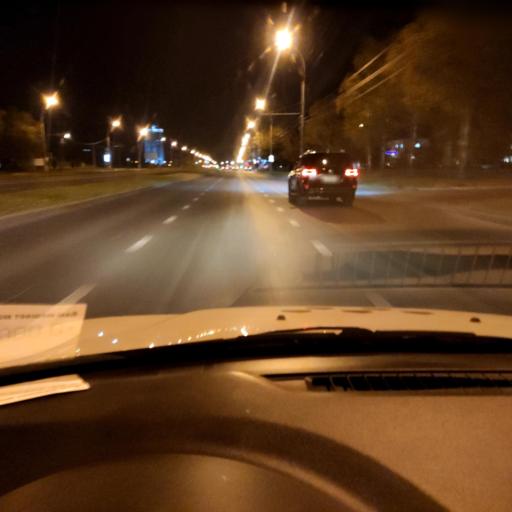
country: RU
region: Samara
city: Tol'yatti
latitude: 53.5439
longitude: 49.2650
